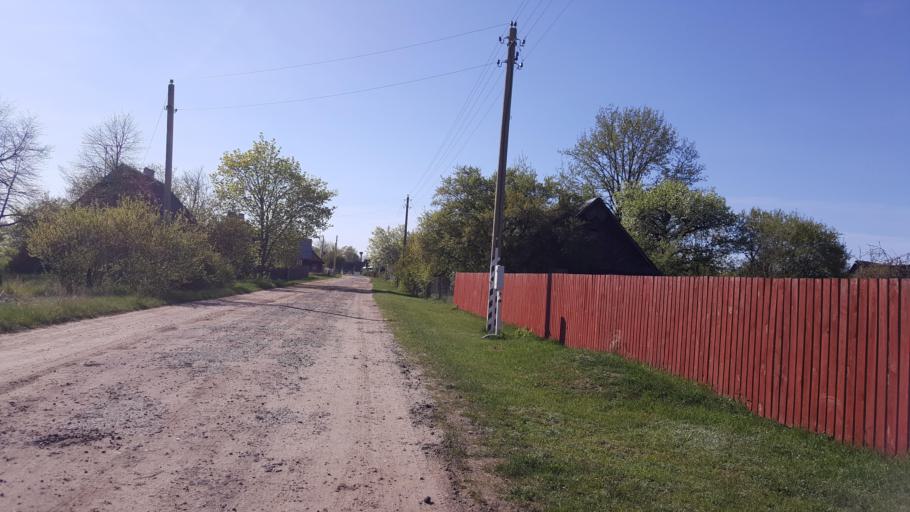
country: BY
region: Brest
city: Kamyanyets
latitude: 52.4395
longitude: 23.8954
